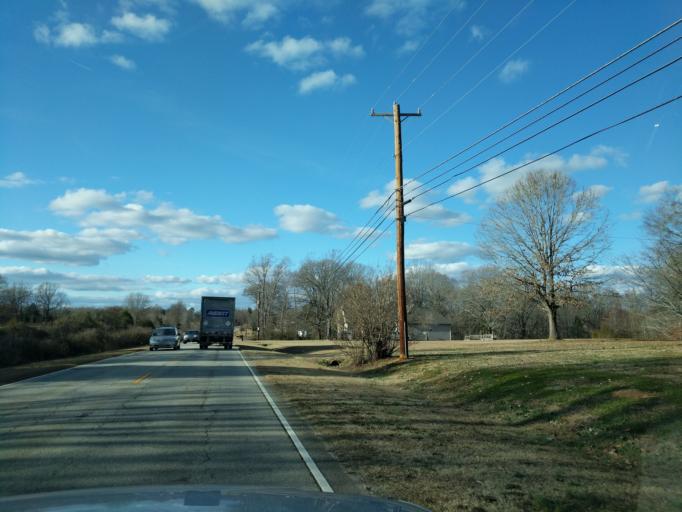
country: US
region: South Carolina
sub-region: Spartanburg County
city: Woodruff
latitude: 34.7113
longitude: -82.0179
